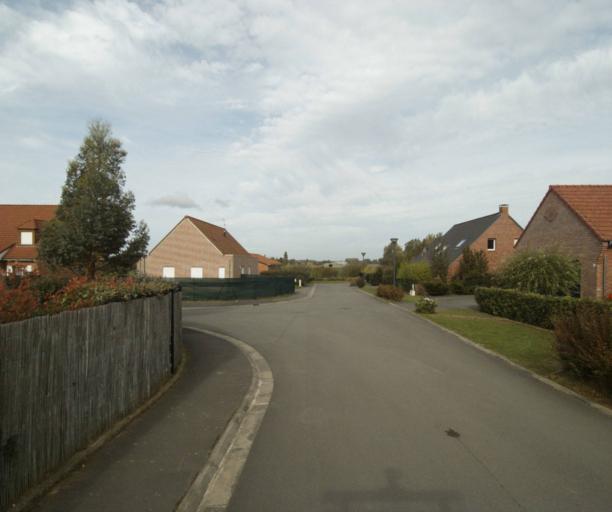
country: FR
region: Nord-Pas-de-Calais
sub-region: Departement du Nord
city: Radinghem-en-Weppes
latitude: 50.6182
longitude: 2.8846
